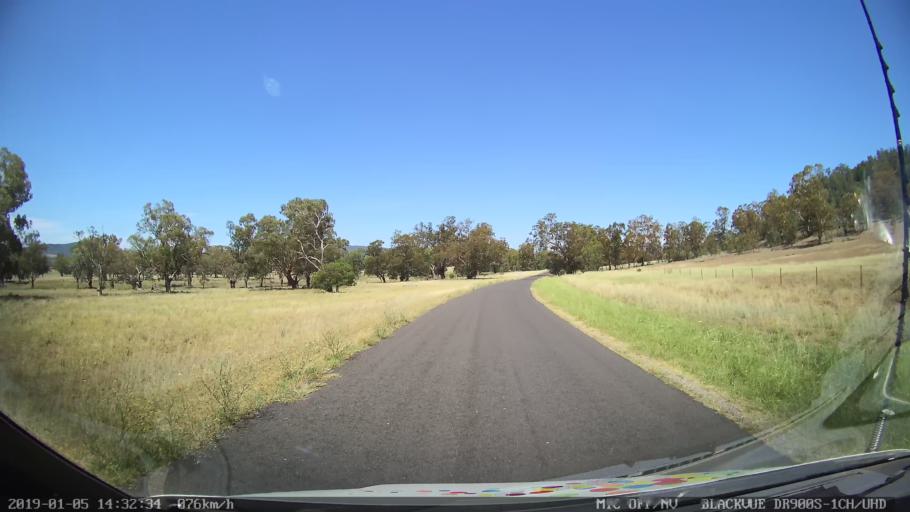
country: AU
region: New South Wales
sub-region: Tamworth Municipality
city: Phillip
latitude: -31.2210
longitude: 150.6199
